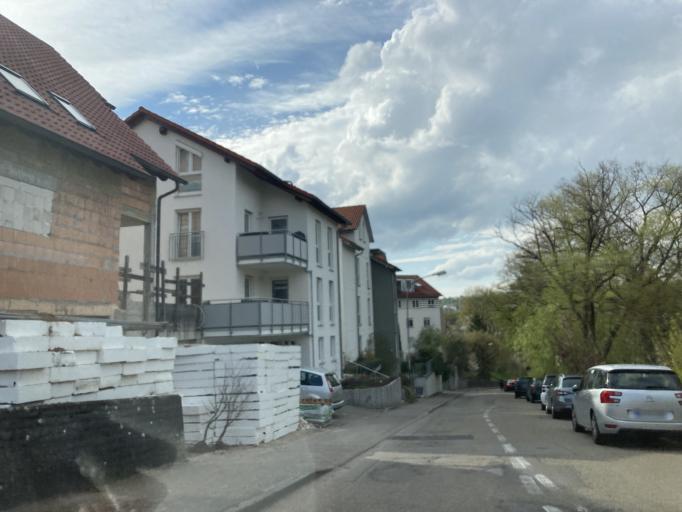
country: DE
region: Baden-Wuerttemberg
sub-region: Tuebingen Region
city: Dettenhausen
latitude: 48.6060
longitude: 9.1023
